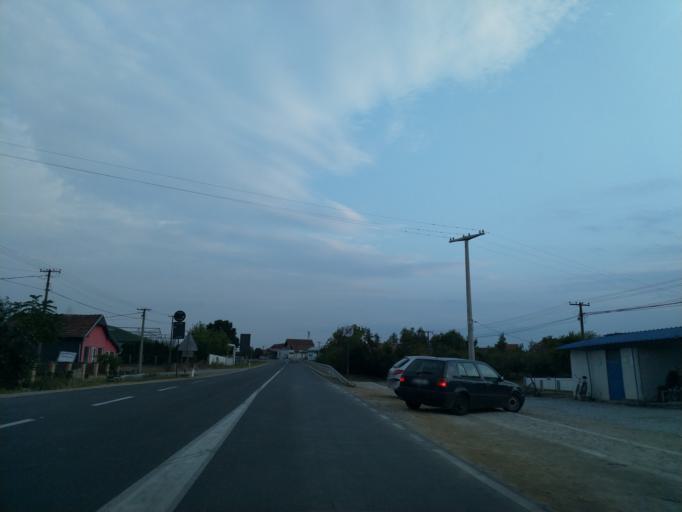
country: RS
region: Central Serbia
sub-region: Sumadijski Okrug
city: Kragujevac
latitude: 44.0928
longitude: 20.8639
